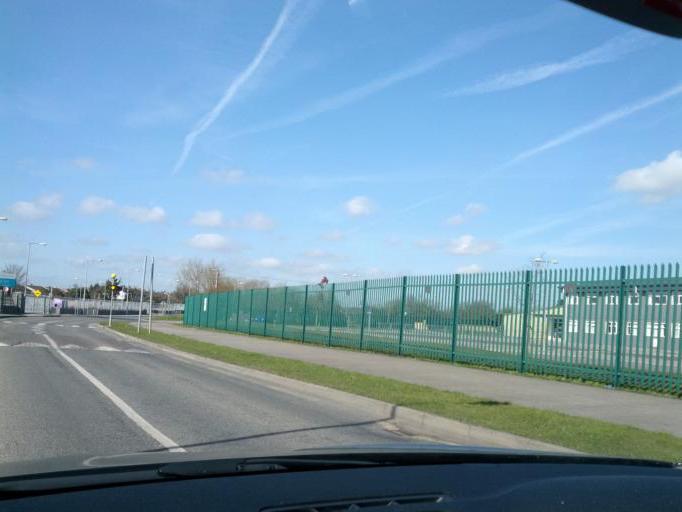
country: IE
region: Leinster
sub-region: Kildare
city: Maynooth
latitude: 53.3696
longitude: -6.5801
